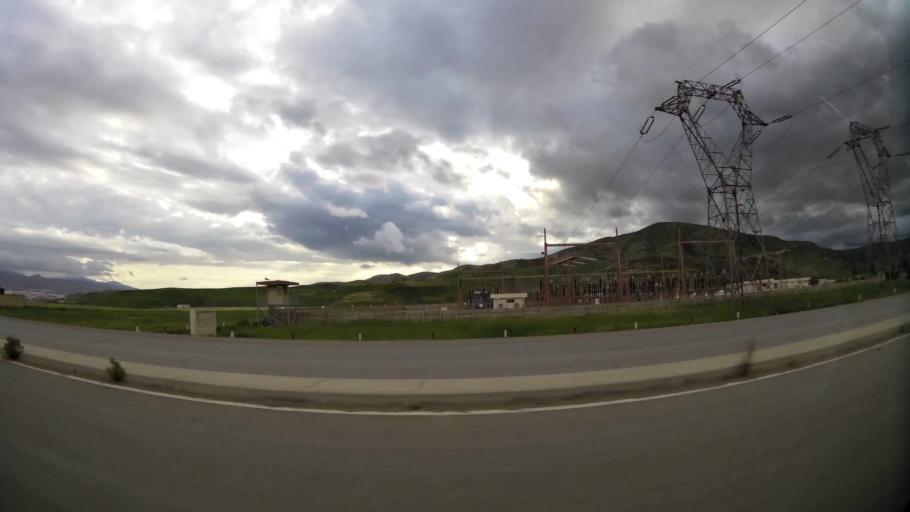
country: MA
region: Taza-Al Hoceima-Taounate
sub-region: Taza
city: Taza
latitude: 34.2683
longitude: -3.9569
